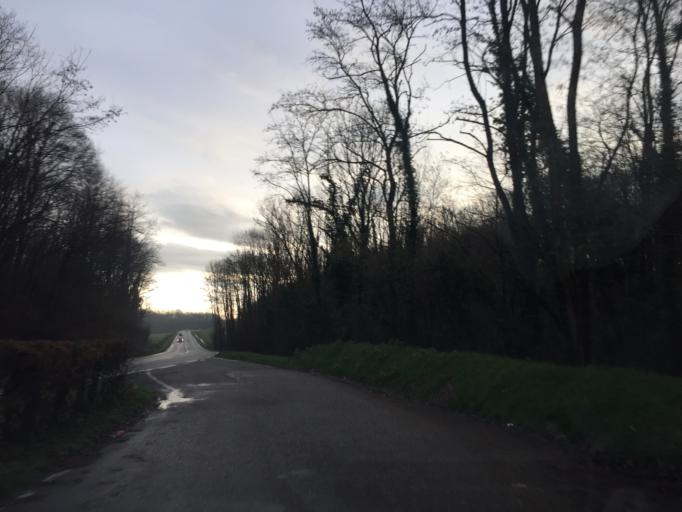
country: FR
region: Franche-Comte
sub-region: Departement du Jura
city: Choisey
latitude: 47.0038
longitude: 5.5054
